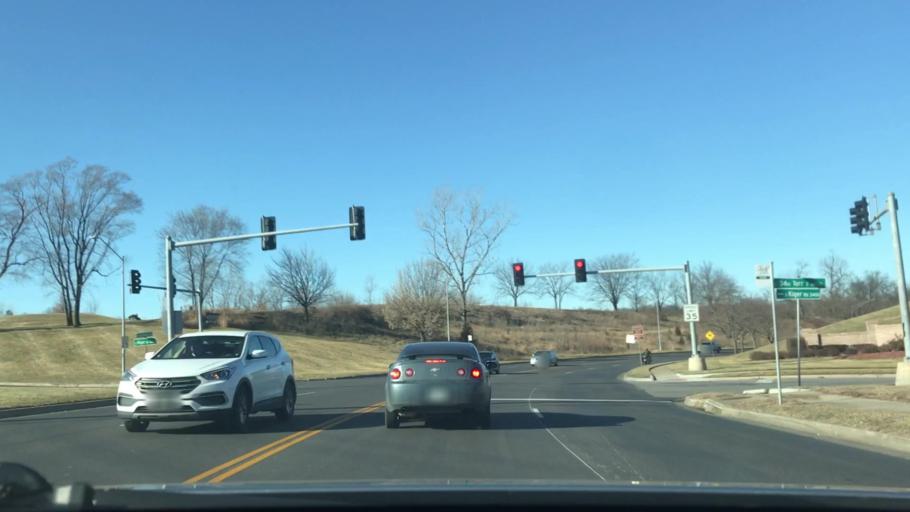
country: US
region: Missouri
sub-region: Jackson County
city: Independence
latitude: 39.0565
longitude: -94.3906
